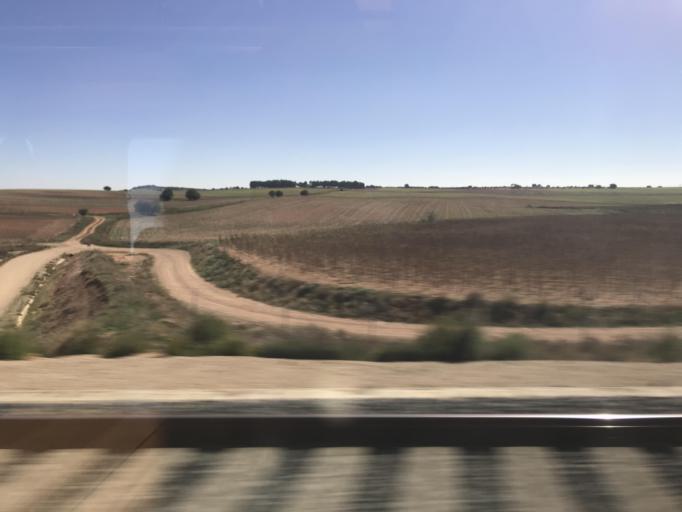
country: ES
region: Castille-La Mancha
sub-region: Provincia de Cuenca
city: Tribaldos
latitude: 40.0045
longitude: -2.9304
